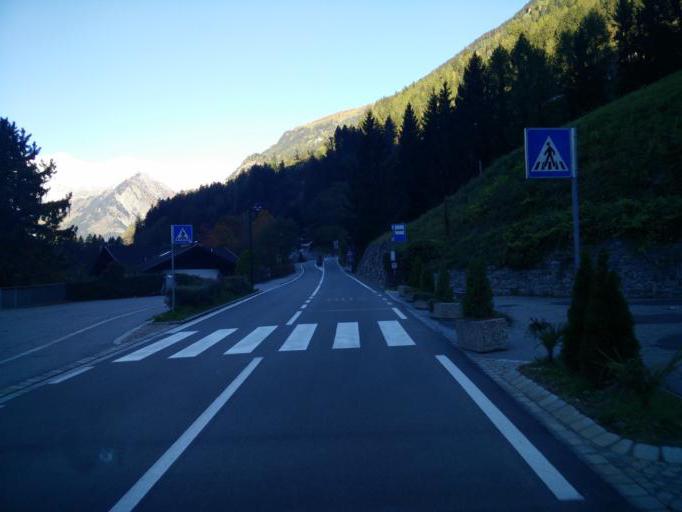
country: IT
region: Trentino-Alto Adige
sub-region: Bolzano
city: San Leonardo in Passiria
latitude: 46.8162
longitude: 11.2422
